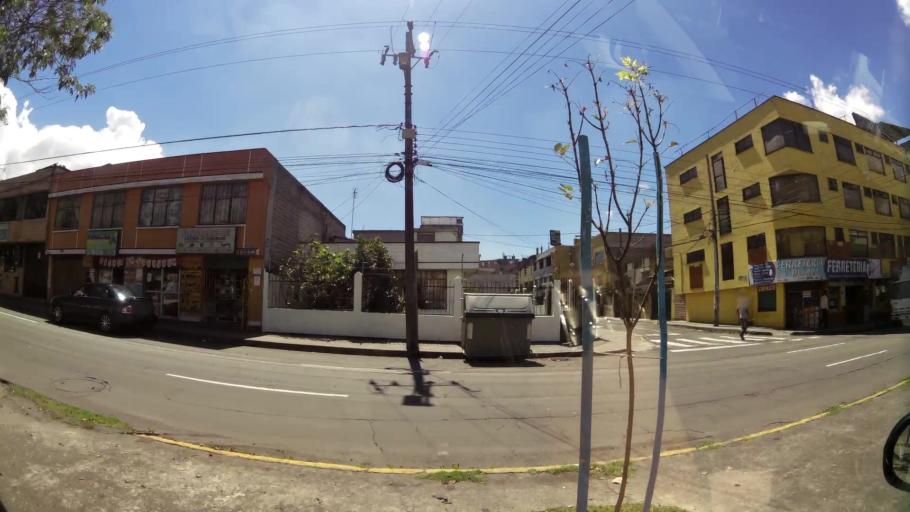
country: EC
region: Pichincha
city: Quito
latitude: -0.2743
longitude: -78.5410
